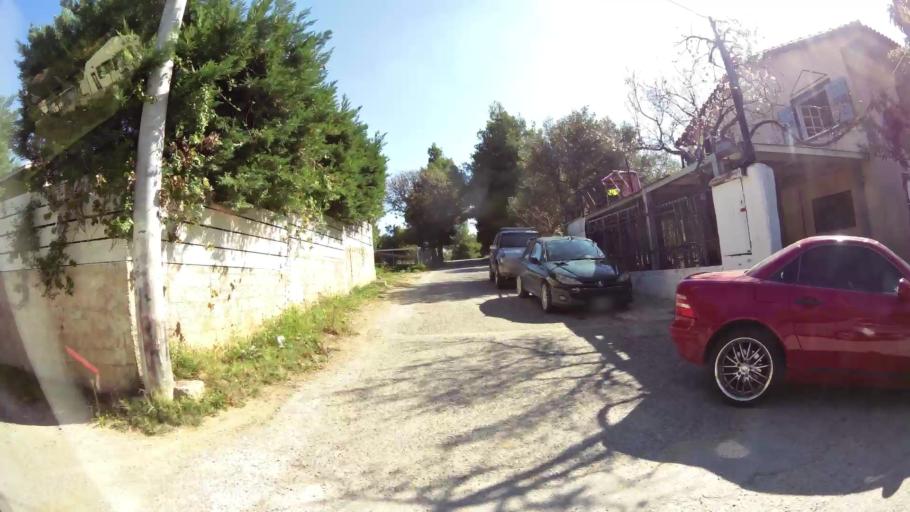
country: GR
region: Attica
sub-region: Nomarchia Athinas
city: Lykovrysi
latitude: 38.0857
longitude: 23.7743
